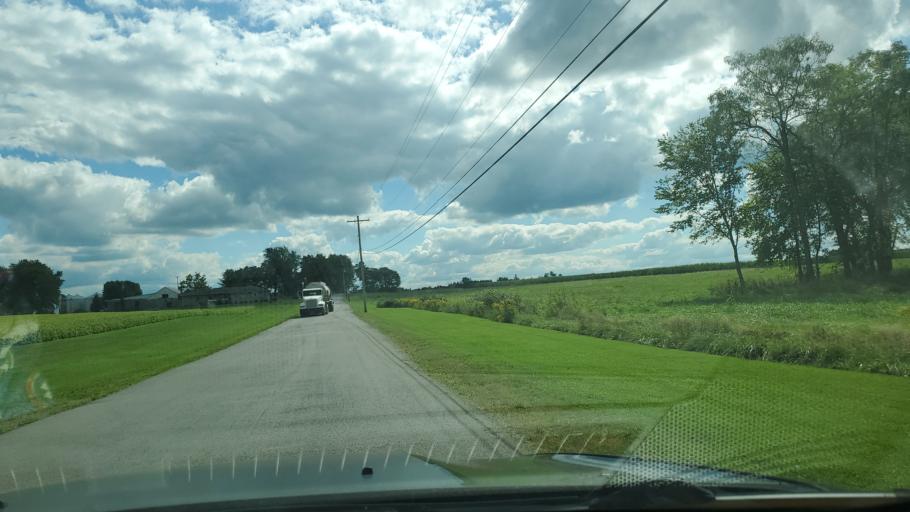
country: US
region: Ohio
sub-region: Mahoning County
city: New Middletown
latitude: 40.9877
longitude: -80.5903
